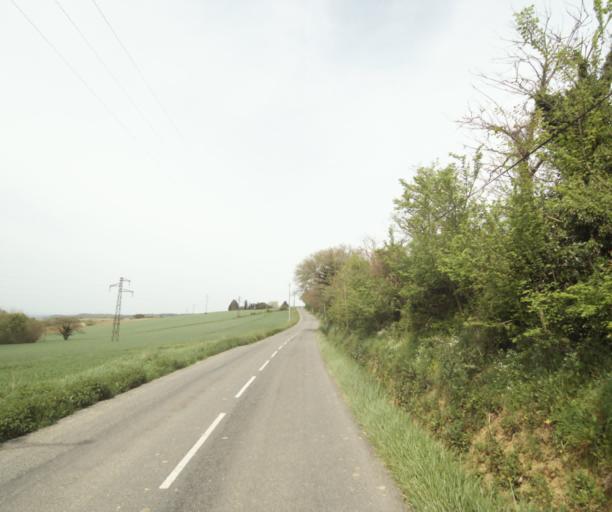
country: FR
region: Midi-Pyrenees
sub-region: Departement de la Haute-Garonne
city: Pechabou
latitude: 43.4961
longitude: 1.4884
